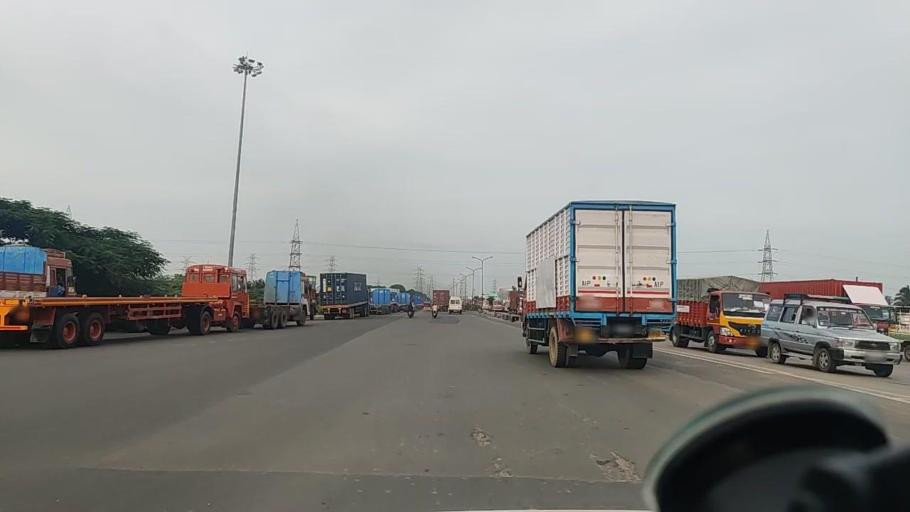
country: IN
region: Tamil Nadu
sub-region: Thiruvallur
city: Chinnasekkadu
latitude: 13.1768
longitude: 80.2451
